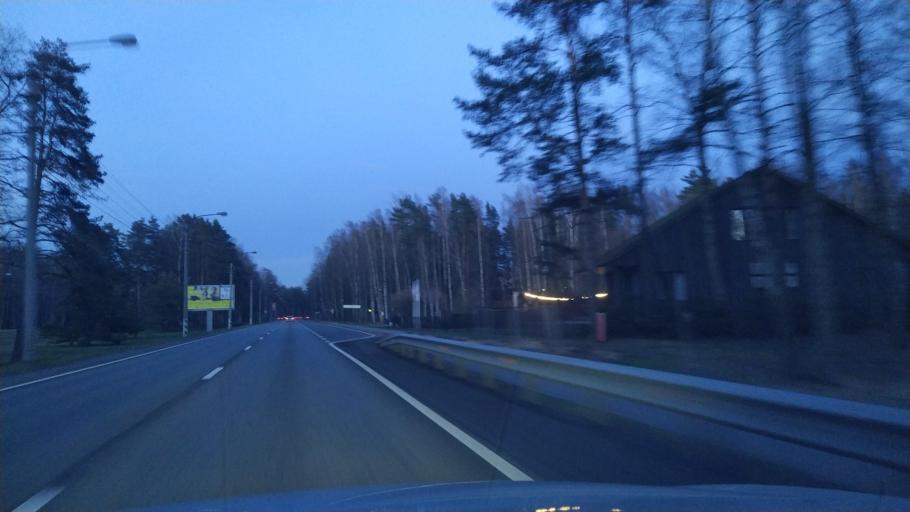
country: RU
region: St.-Petersburg
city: Ol'gino
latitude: 59.9976
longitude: 30.1018
